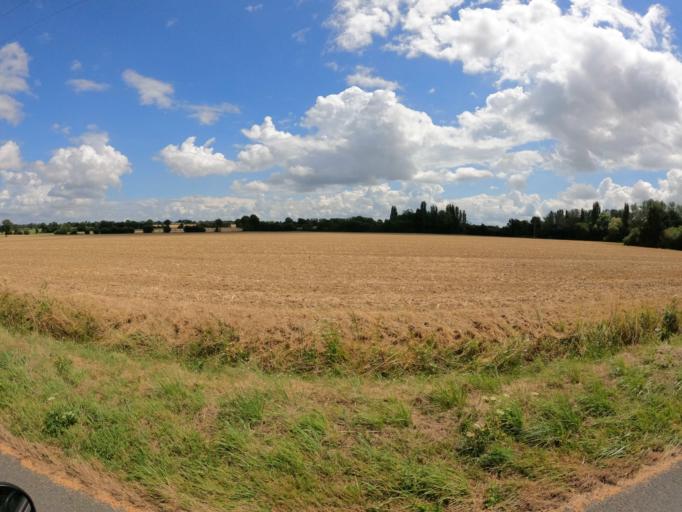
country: FR
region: Pays de la Loire
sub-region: Departement de Maine-et-Loire
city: Mire
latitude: 47.7352
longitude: -0.5124
